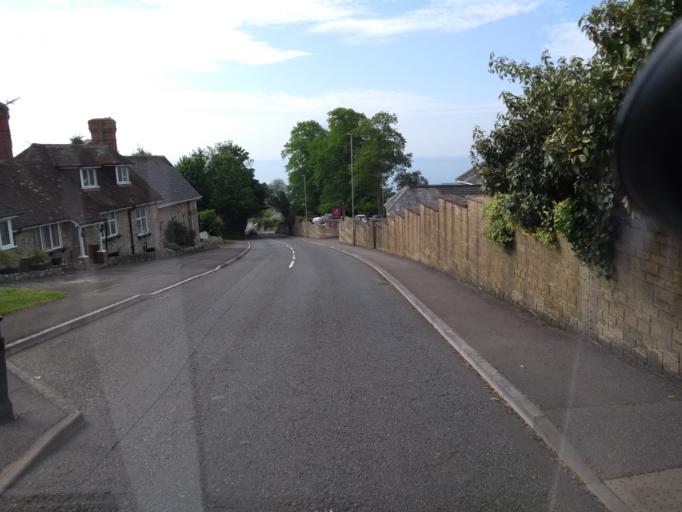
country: GB
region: England
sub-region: Dorset
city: Lyme Regis
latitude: 50.7330
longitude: -2.9325
